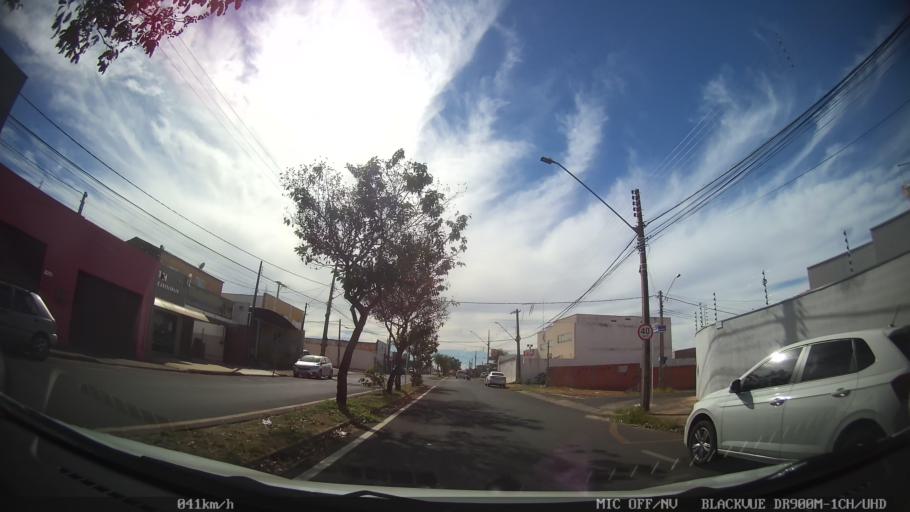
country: BR
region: Sao Paulo
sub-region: Catanduva
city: Catanduva
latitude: -21.1229
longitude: -48.9457
